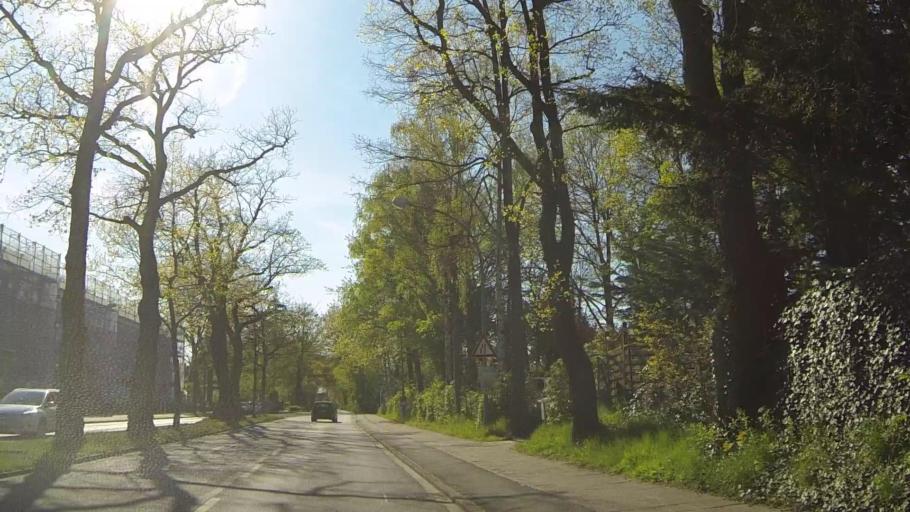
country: DE
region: Schleswig-Holstein
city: Rellingen
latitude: 53.6448
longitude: 9.8026
